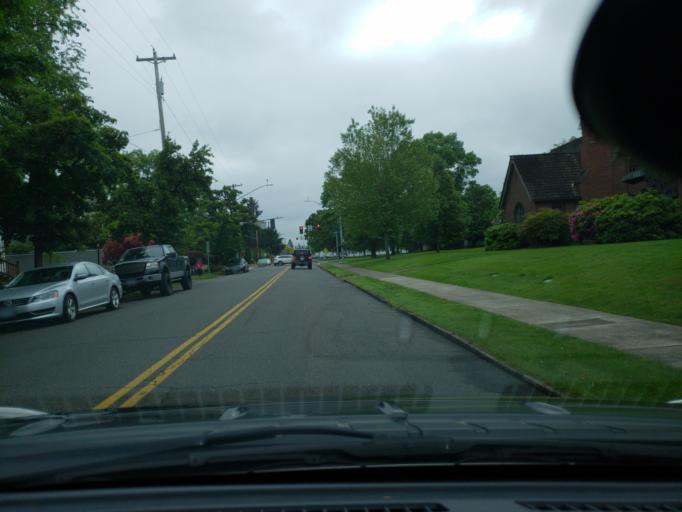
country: US
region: Oregon
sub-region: Marion County
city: Salem
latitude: 44.9470
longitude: -123.0273
